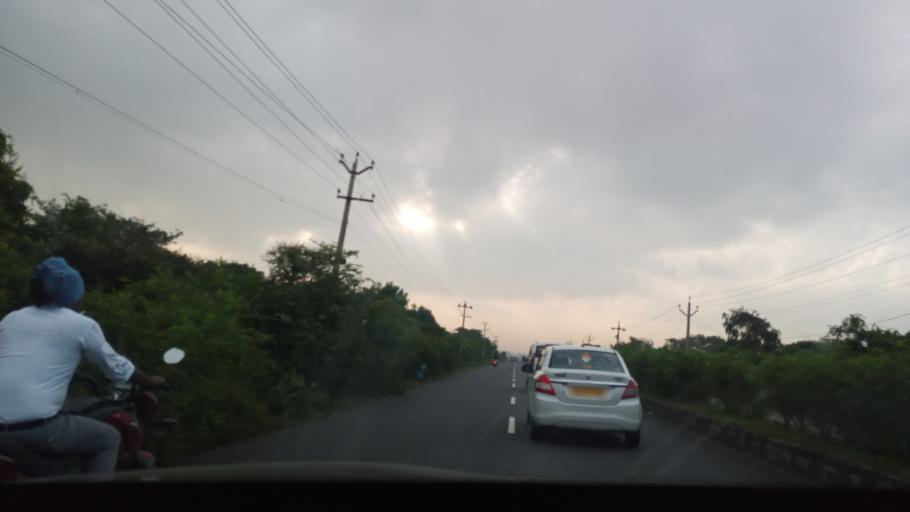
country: IN
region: Tamil Nadu
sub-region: Kancheepuram
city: Vengavasal
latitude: 12.8151
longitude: 80.1789
